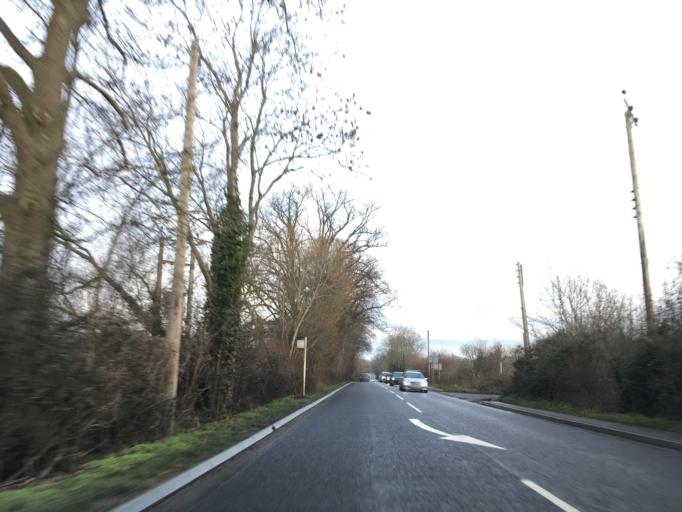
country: GB
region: England
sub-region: Gloucestershire
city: Shurdington
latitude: 51.8546
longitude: -2.1319
